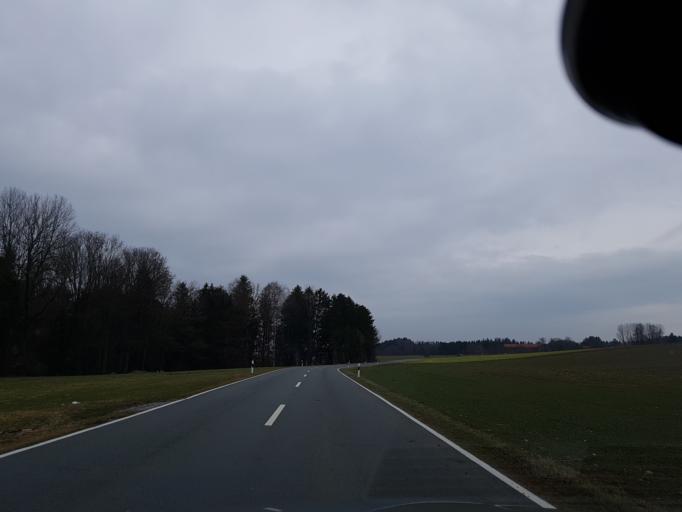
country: DE
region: Bavaria
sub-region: Upper Bavaria
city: Feldkirchen-Westerham
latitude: 47.9388
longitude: 11.8663
